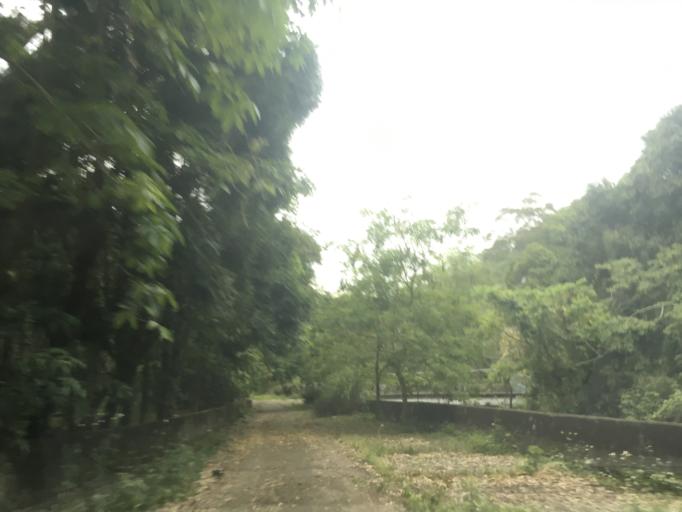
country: TW
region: Taiwan
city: Zhongxing New Village
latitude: 24.0345
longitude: 120.7833
